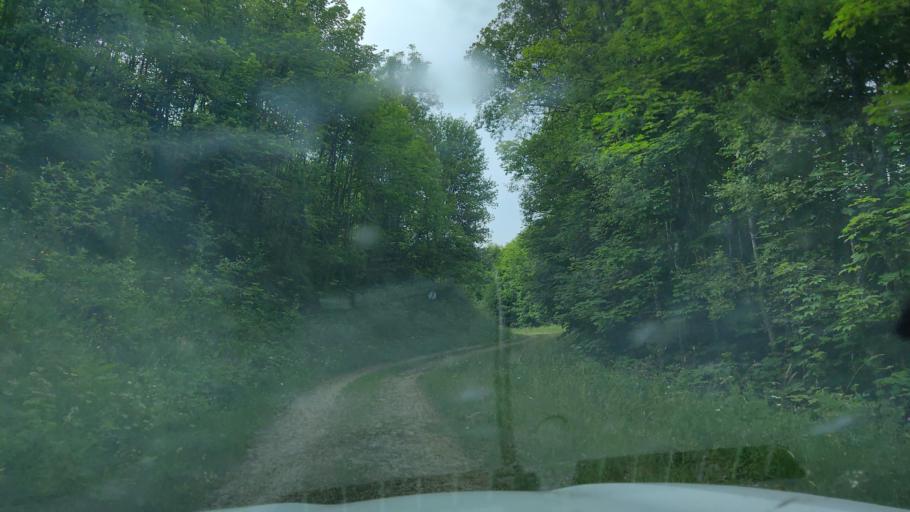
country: FR
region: Rhone-Alpes
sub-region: Departement de la Savoie
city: Cruet
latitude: 45.5950
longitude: 6.1056
